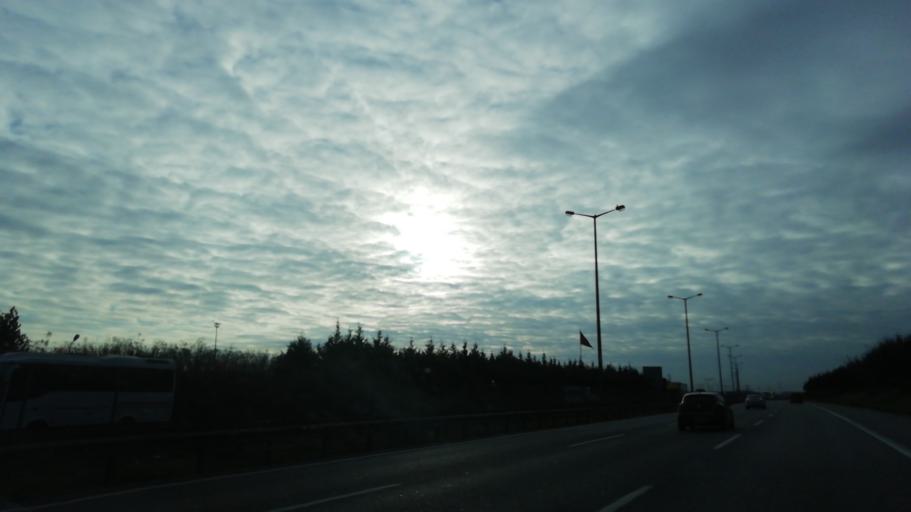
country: TR
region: Istanbul
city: Icmeler
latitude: 40.9192
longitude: 29.3520
